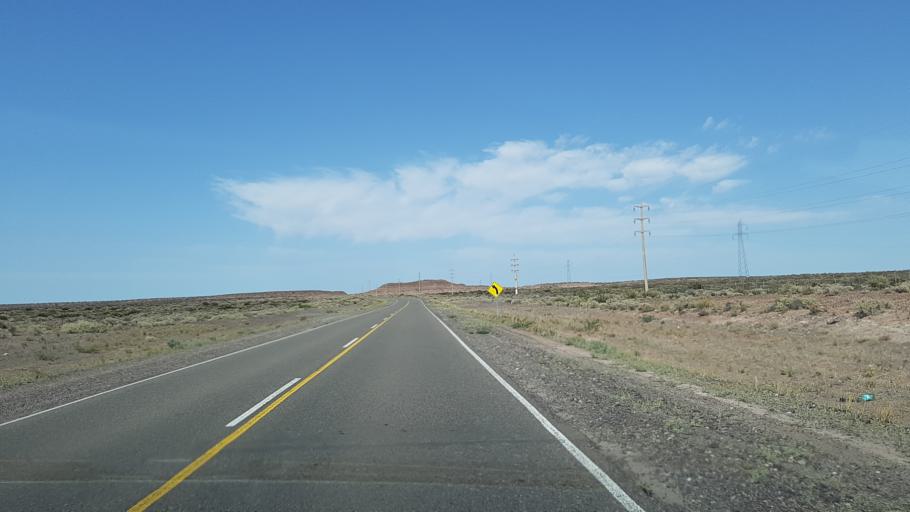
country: AR
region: Neuquen
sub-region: Departamento de Picun Leufu
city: Picun Leufu
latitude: -39.3997
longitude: -69.1227
